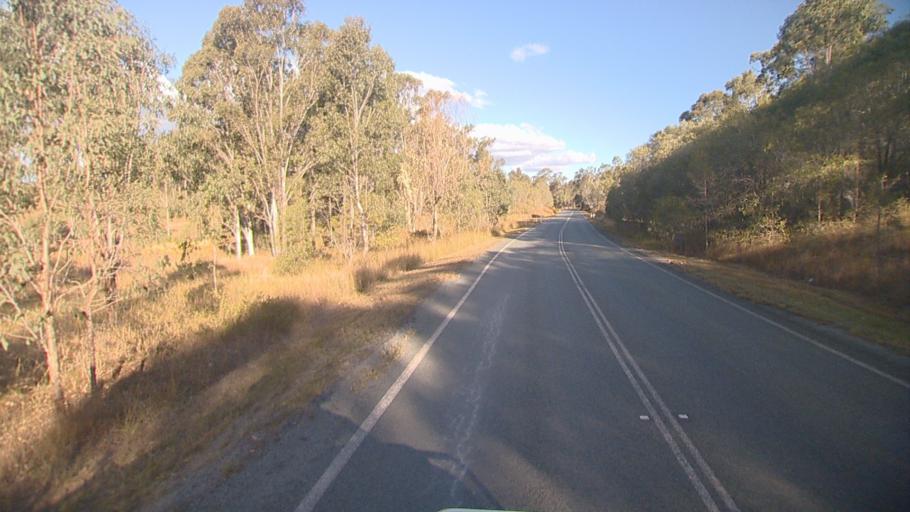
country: AU
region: Queensland
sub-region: Logan
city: Cedar Vale
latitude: -27.8946
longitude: 153.0878
